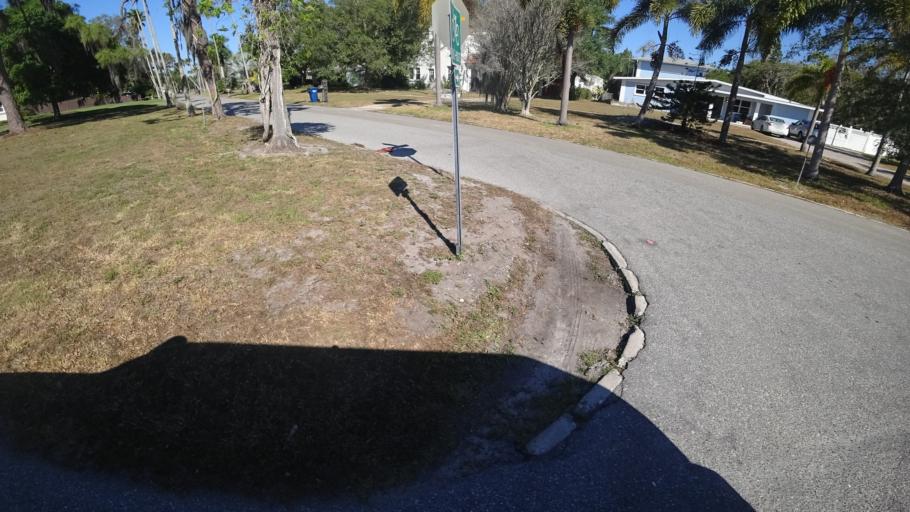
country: US
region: Florida
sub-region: Manatee County
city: West Bradenton
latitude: 27.4949
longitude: -82.6380
